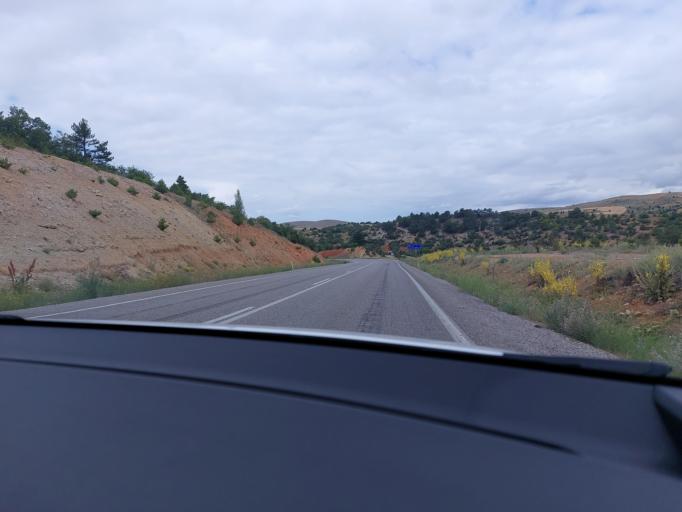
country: TR
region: Konya
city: Doganbey
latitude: 37.8979
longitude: 31.8079
